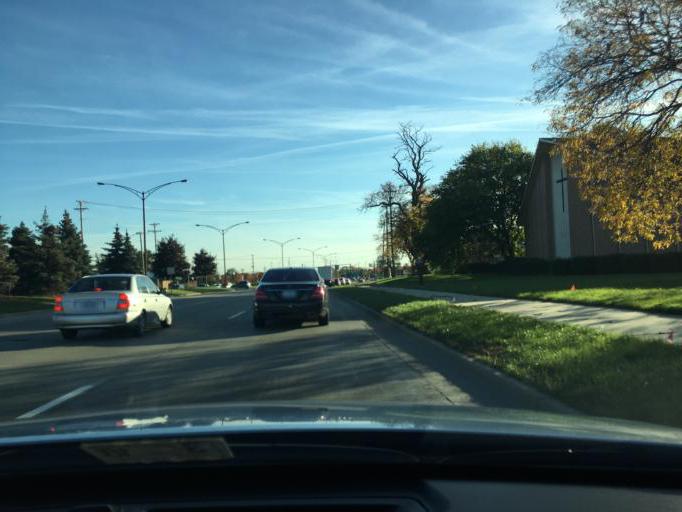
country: US
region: Michigan
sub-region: Oakland County
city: Clawson
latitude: 42.5664
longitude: -83.1281
